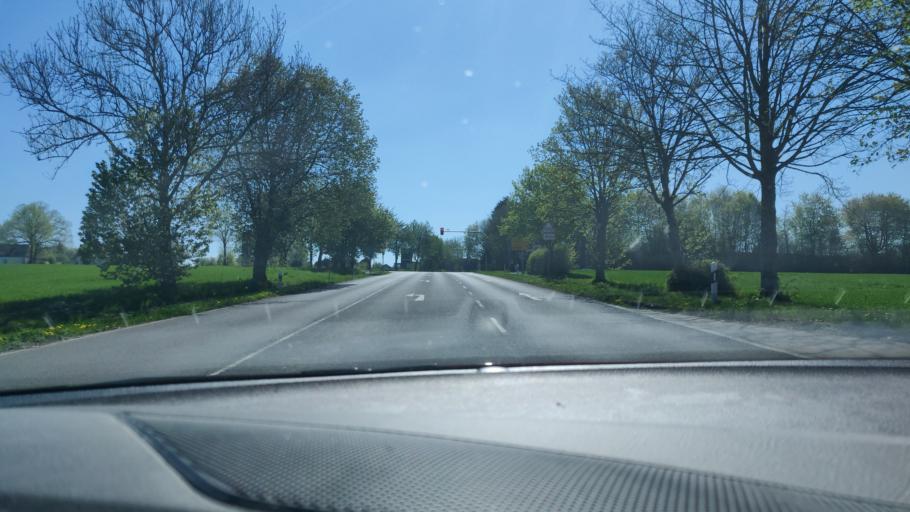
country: DE
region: North Rhine-Westphalia
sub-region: Regierungsbezirk Dusseldorf
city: Mettmann
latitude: 51.2340
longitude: 6.9964
